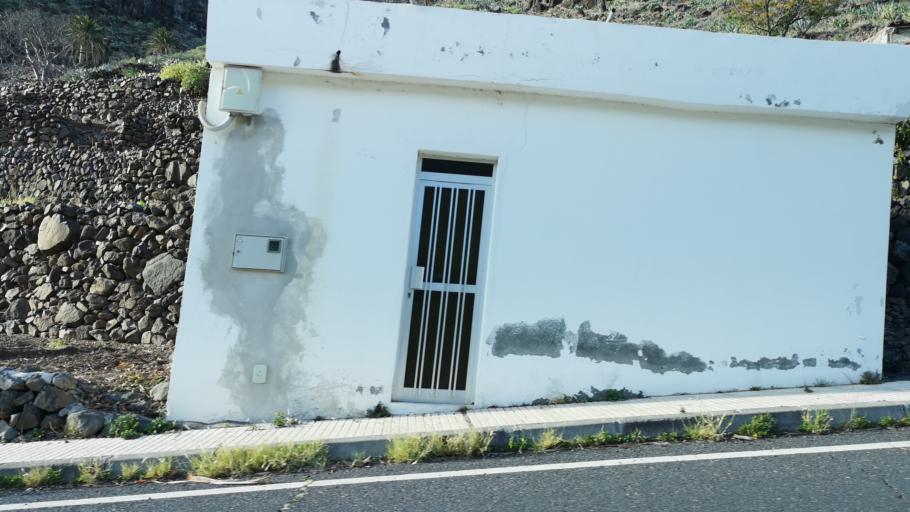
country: ES
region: Canary Islands
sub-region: Provincia de Santa Cruz de Tenerife
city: Vallehermosa
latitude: 28.1116
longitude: -17.3190
